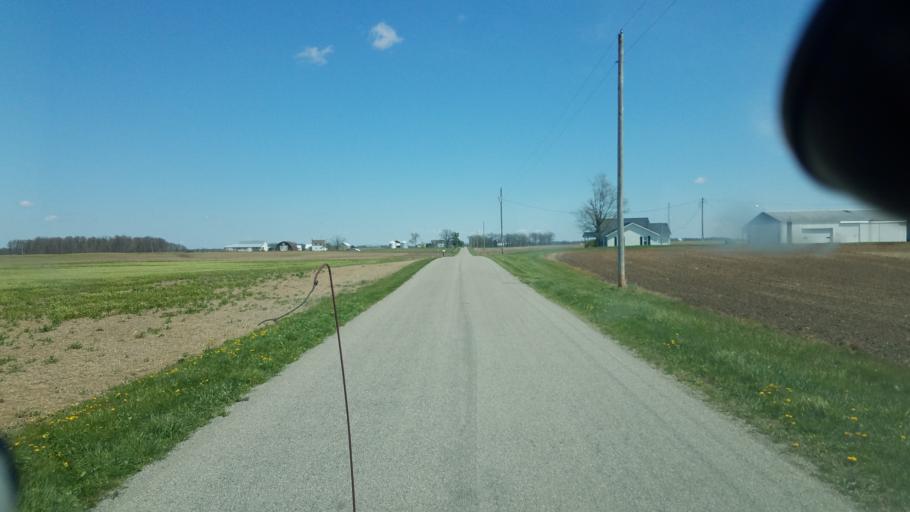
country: US
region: Ohio
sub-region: Union County
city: Richwood
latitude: 40.4923
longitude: -83.2735
